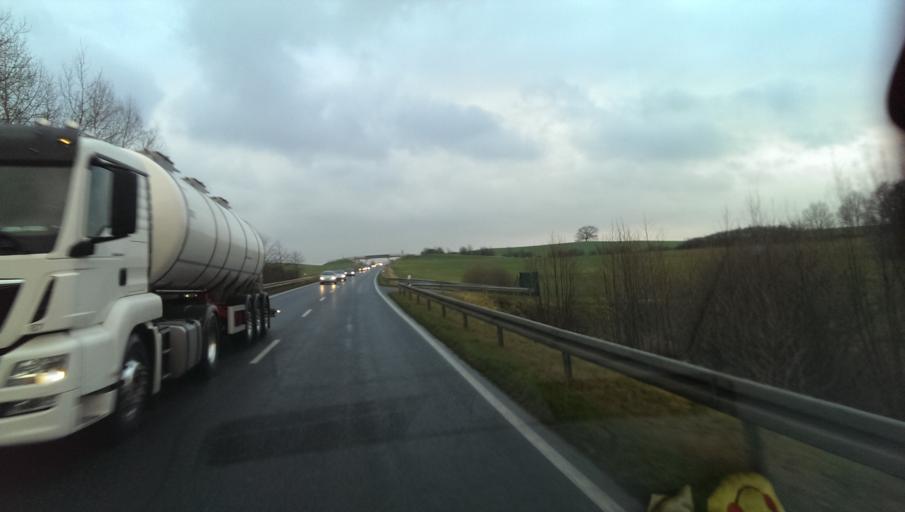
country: DE
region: Saxony
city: Moritzburg
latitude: 51.1480
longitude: 13.6483
